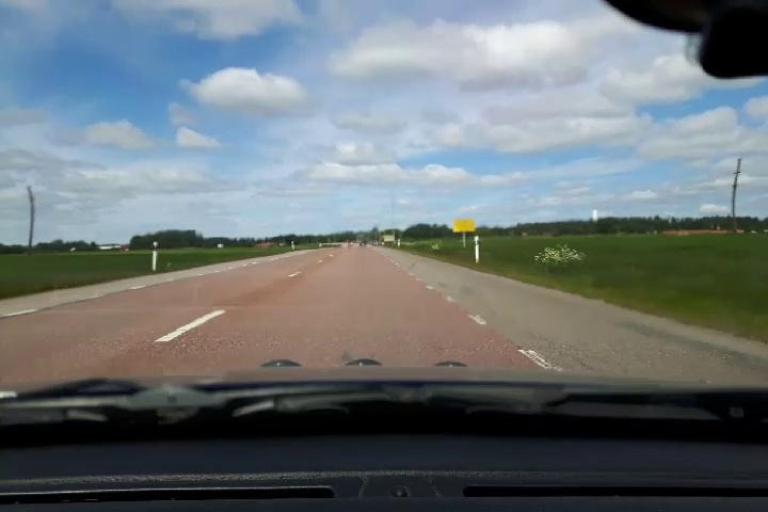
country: SE
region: Uppsala
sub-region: Osthammars Kommun
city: Bjorklinge
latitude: 60.0149
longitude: 17.5580
